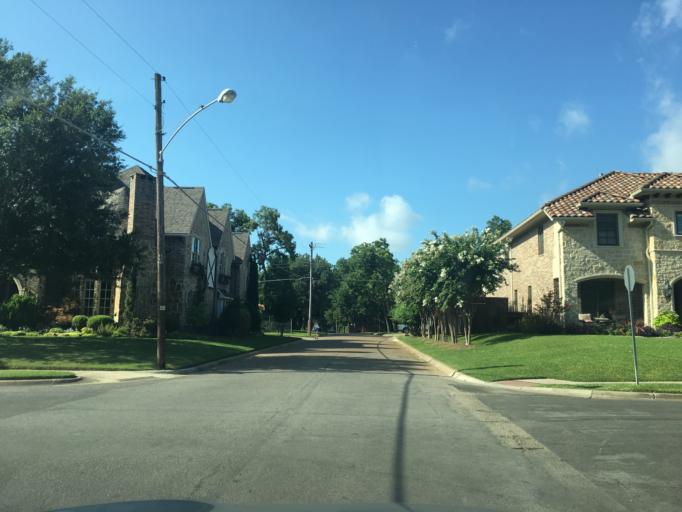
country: US
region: Texas
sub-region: Dallas County
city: Highland Park
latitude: 32.8333
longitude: -96.7471
